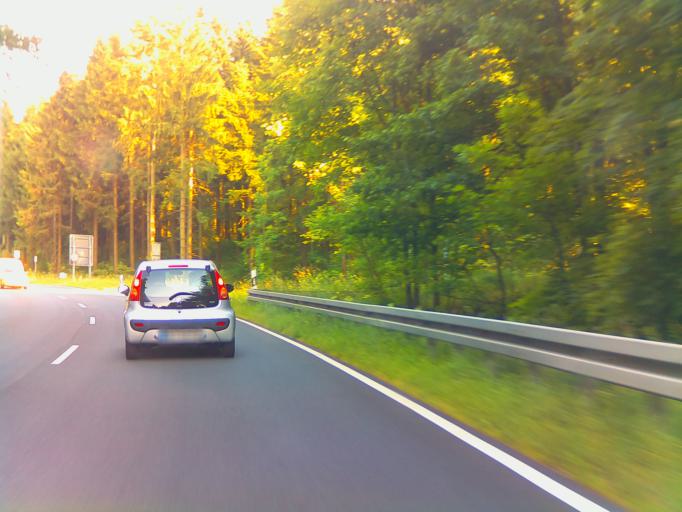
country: DE
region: Hesse
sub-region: Regierungsbezirk Kassel
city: Gersfeld
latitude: 50.4233
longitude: 9.9338
